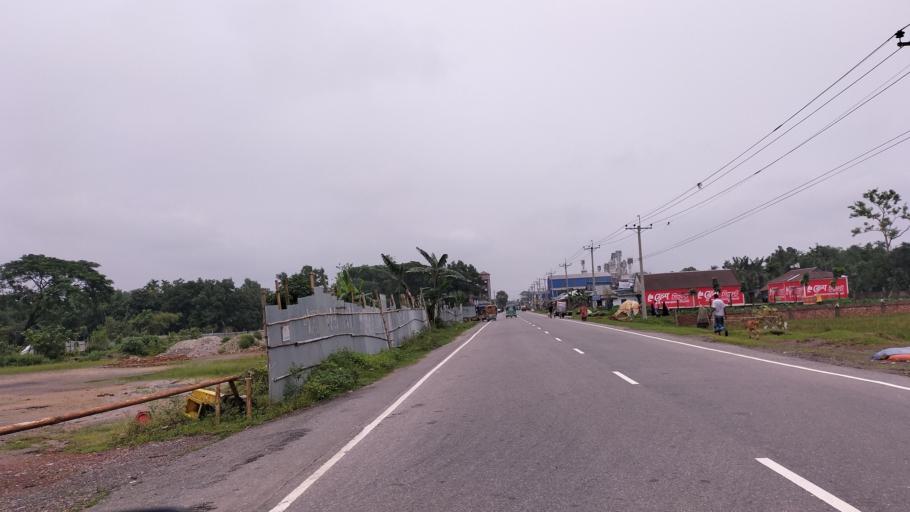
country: BD
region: Dhaka
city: Netrakona
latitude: 24.8512
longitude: 90.6253
